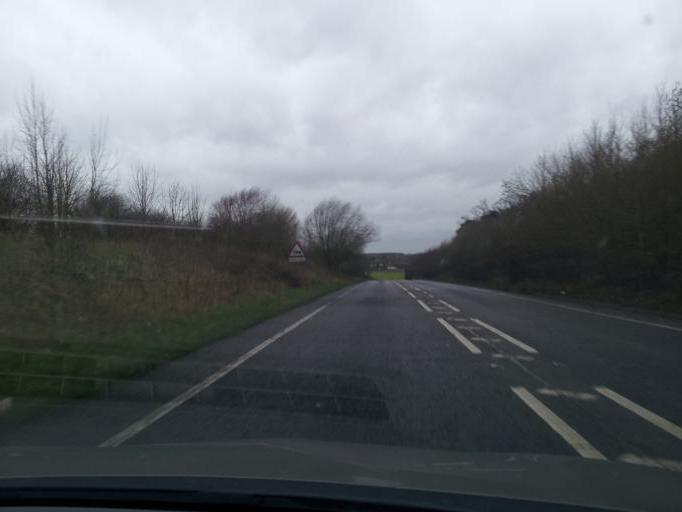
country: GB
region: England
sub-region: Suffolk
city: Botesdale
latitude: 52.3360
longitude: 0.9758
